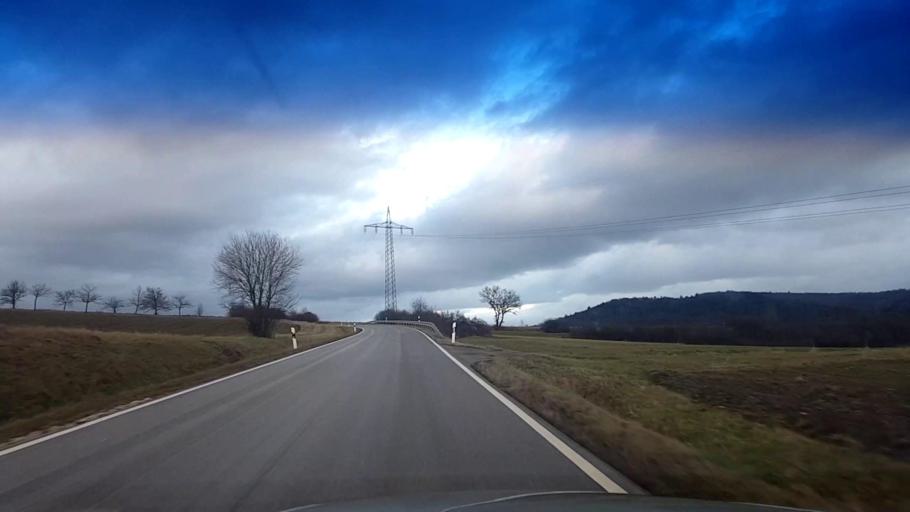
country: DE
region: Bavaria
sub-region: Upper Franconia
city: Litzendorf
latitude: 49.8744
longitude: 11.0045
